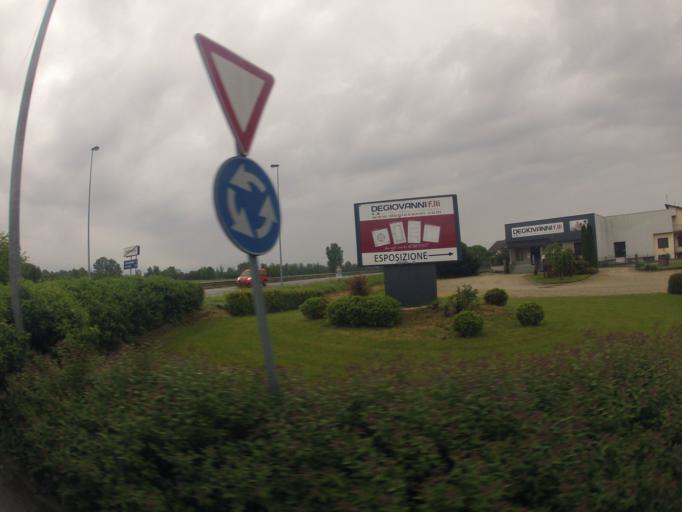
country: IT
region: Piedmont
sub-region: Provincia di Torino
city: Lombriasco
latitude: 44.8437
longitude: 7.6418
